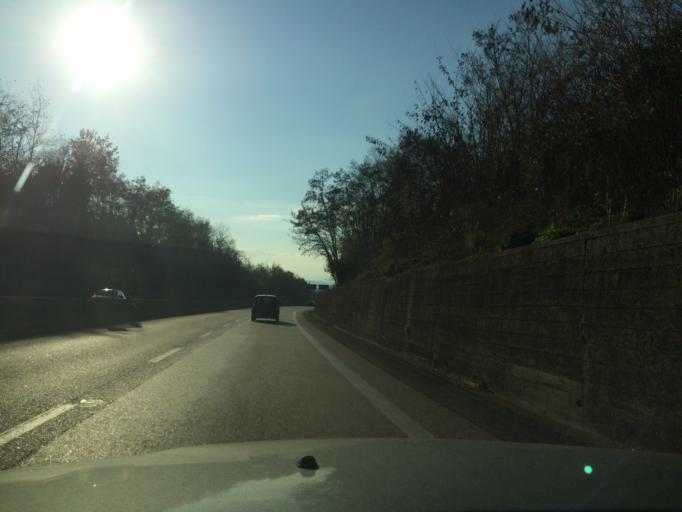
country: IT
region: Umbria
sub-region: Provincia di Terni
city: Fornole
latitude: 42.5332
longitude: 12.4782
